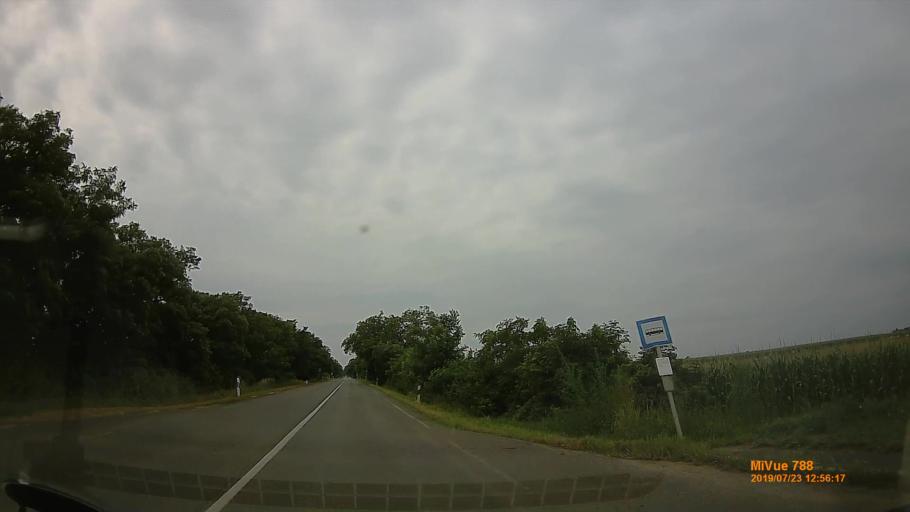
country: HU
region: Szabolcs-Szatmar-Bereg
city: Nagycserkesz
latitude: 47.9570
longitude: 21.5022
